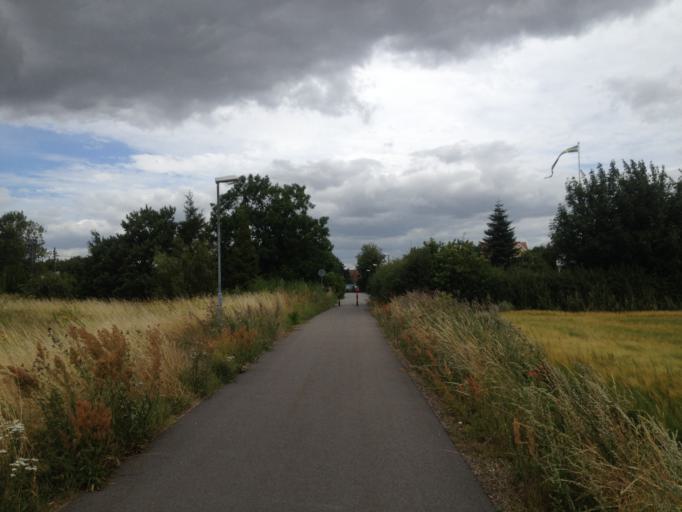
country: SE
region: Skane
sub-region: Lomma Kommun
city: Lomma
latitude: 55.7224
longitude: 13.0750
